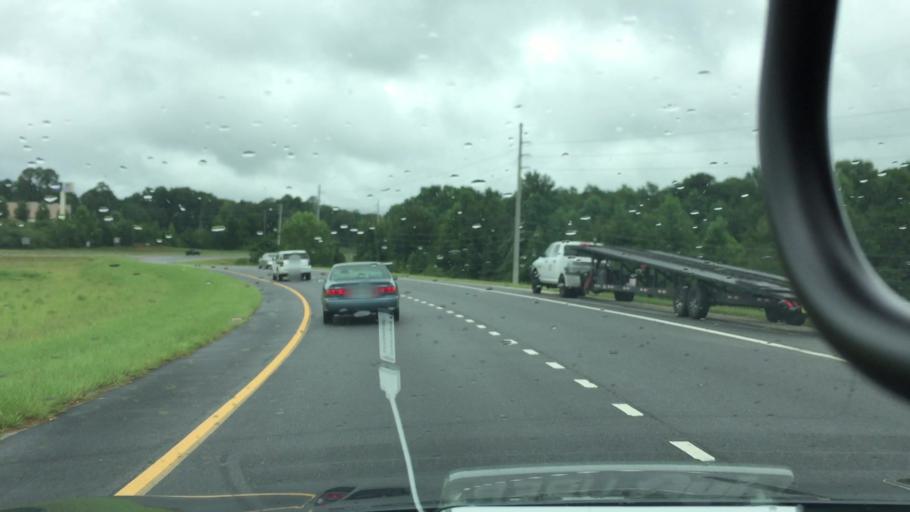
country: US
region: Alabama
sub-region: Lee County
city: Auburn
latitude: 32.6044
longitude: -85.4269
